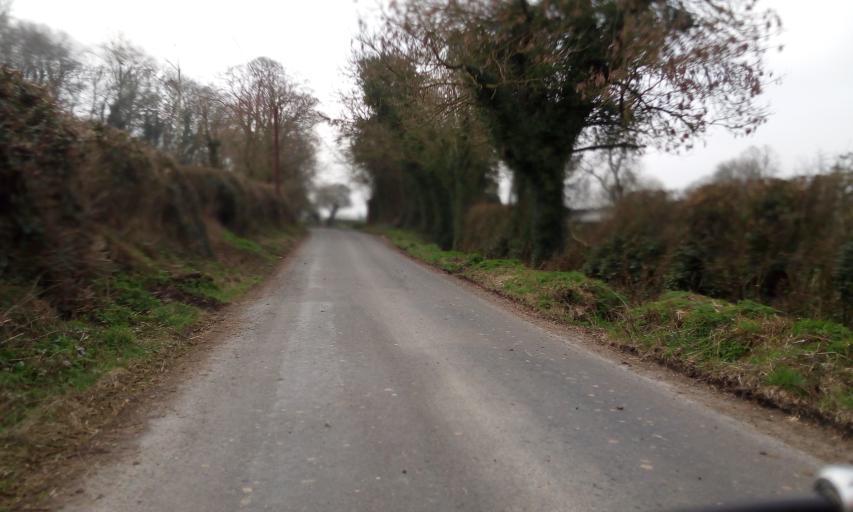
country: IE
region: Leinster
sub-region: Kilkenny
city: Kilkenny
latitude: 52.6655
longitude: -7.1864
